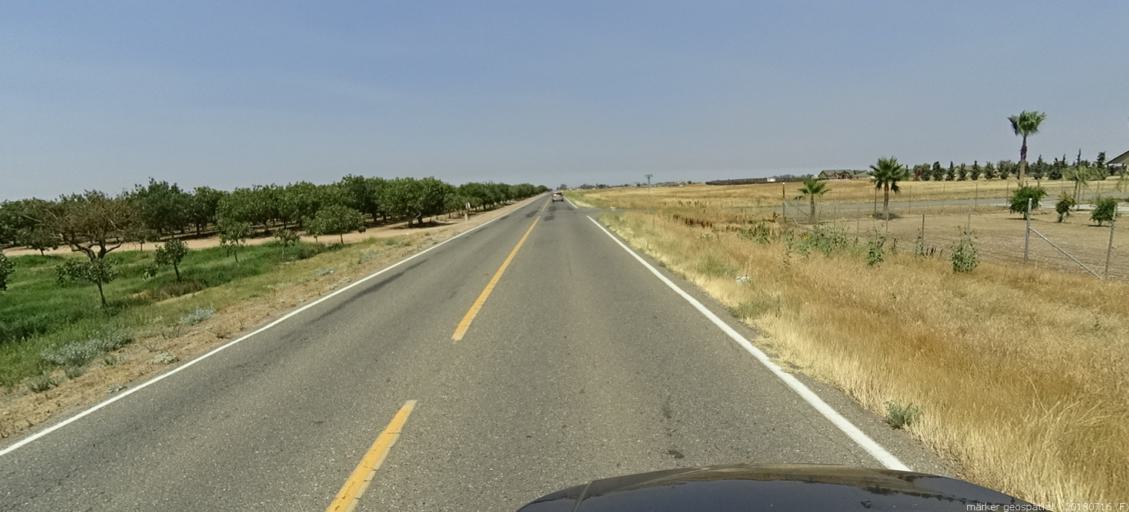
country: US
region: California
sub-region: Madera County
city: Madera Acres
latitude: 37.0541
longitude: -120.0059
